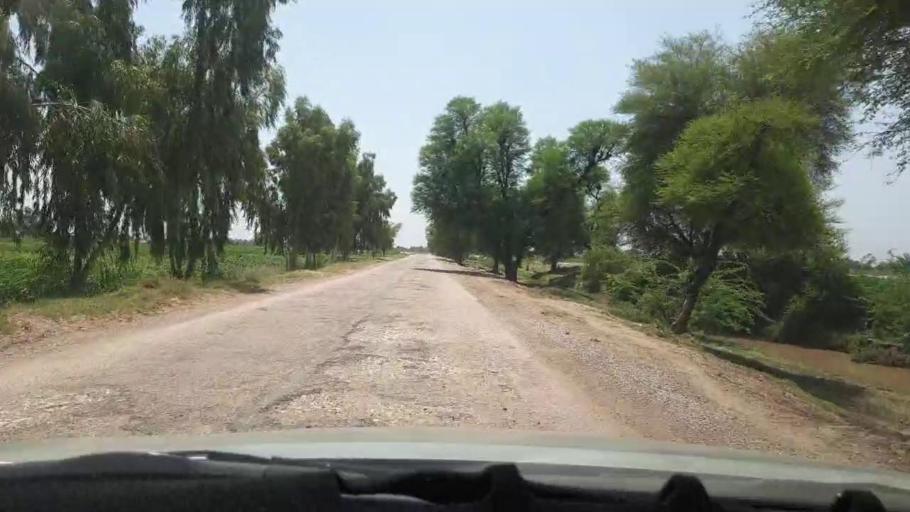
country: PK
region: Sindh
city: Pano Aqil
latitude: 27.7413
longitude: 69.1994
